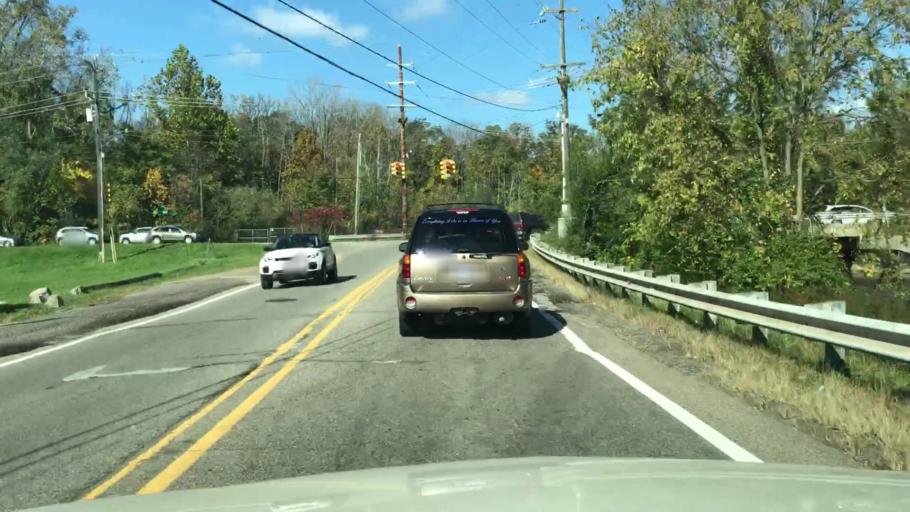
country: US
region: Michigan
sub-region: Oakland County
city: Rochester
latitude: 42.6713
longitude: -83.0963
